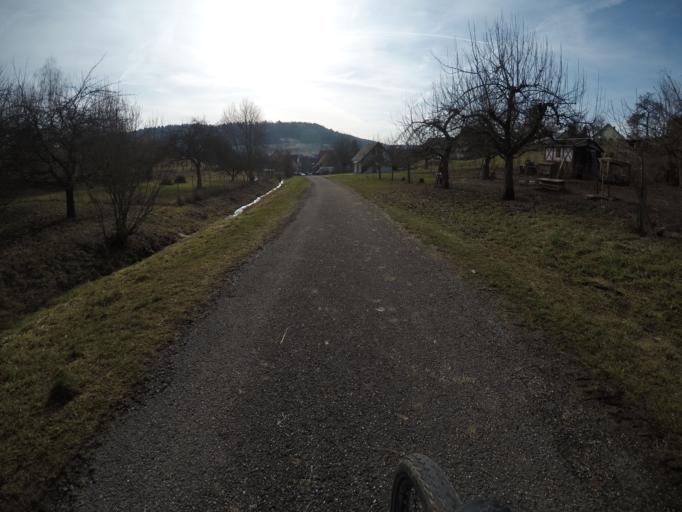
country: DE
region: Baden-Wuerttemberg
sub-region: Karlsruhe Region
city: Wildberg
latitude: 48.6523
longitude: 8.7742
